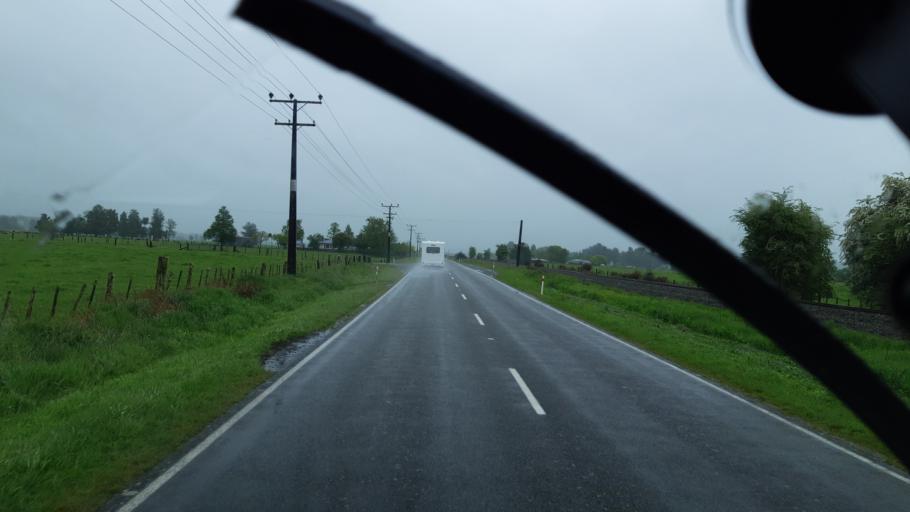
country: NZ
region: West Coast
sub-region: Grey District
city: Greymouth
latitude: -42.2914
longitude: 171.6563
